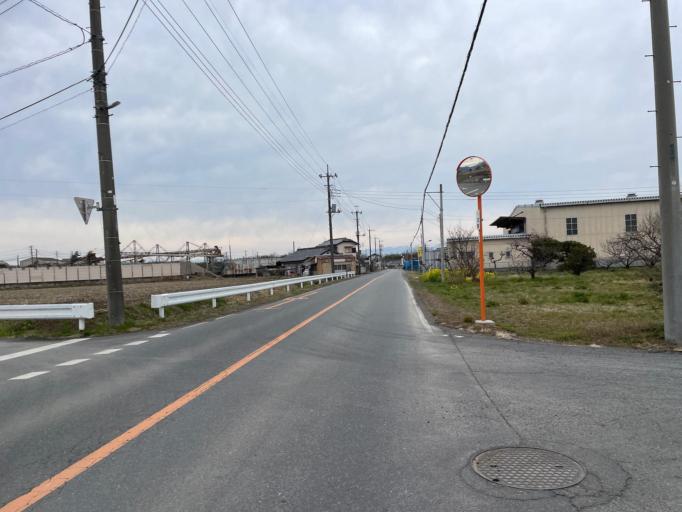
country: JP
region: Gunma
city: Fujioka
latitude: 36.2282
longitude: 139.0994
